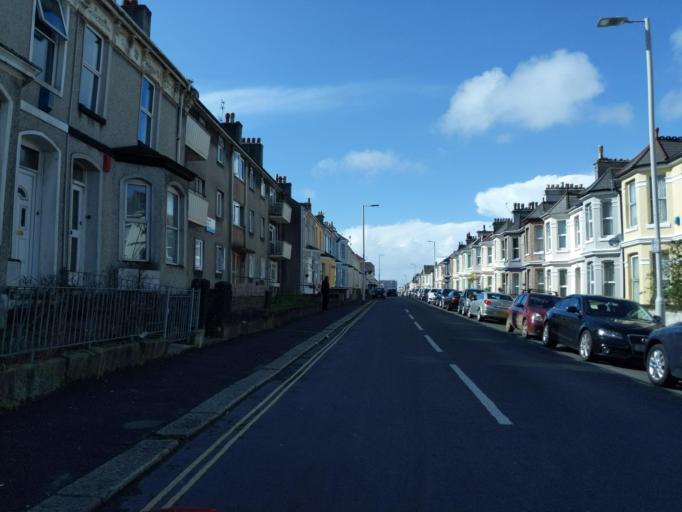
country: GB
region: England
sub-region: Plymouth
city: Plymouth
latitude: 50.3717
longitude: -4.1219
